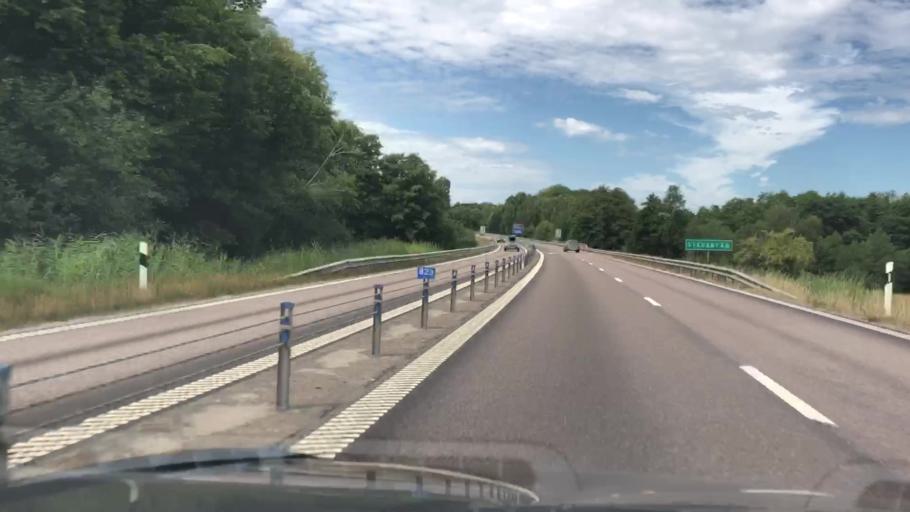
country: SE
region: Blekinge
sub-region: Karlskrona Kommun
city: Rodeby
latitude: 56.2020
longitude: 15.6698
